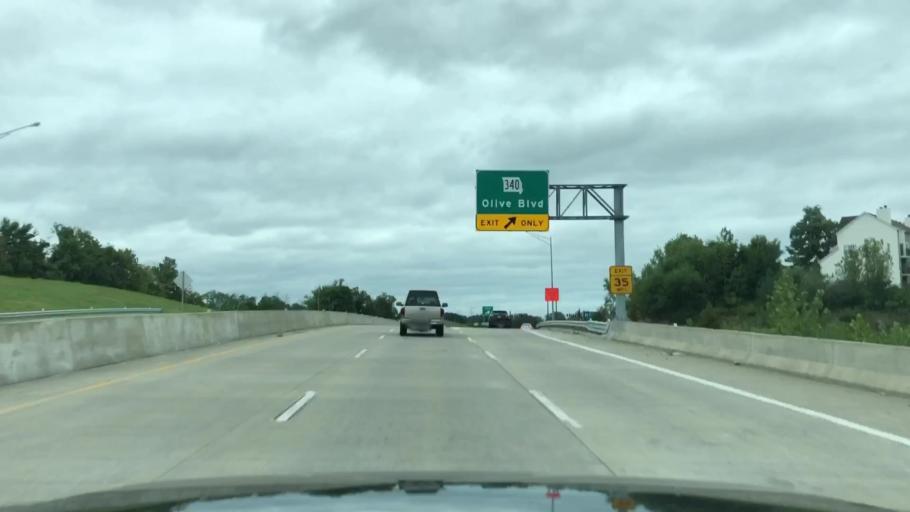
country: US
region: Missouri
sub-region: Saint Louis County
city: Maryland Heights
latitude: 38.6844
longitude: -90.4940
